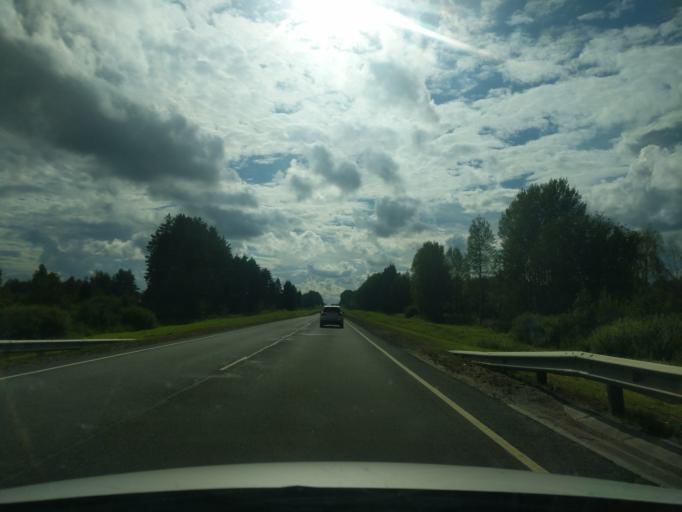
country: RU
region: Jaroslavl
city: Nekrasovskoye
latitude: 57.6244
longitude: 40.3639
